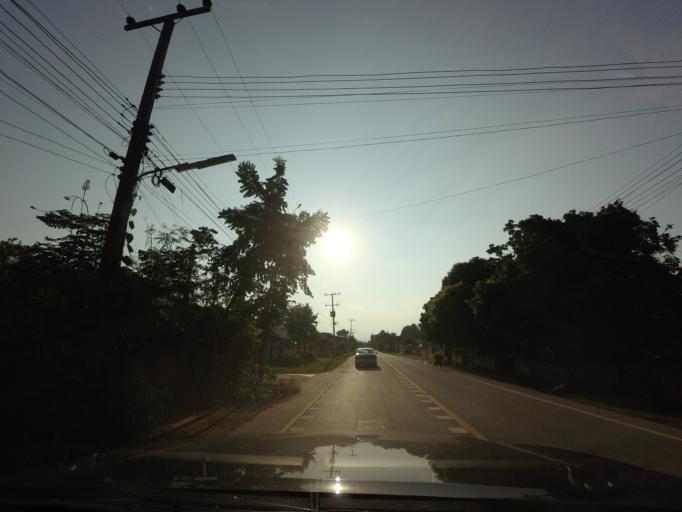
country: TH
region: Nan
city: Na Noi
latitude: 18.3343
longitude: 100.7658
